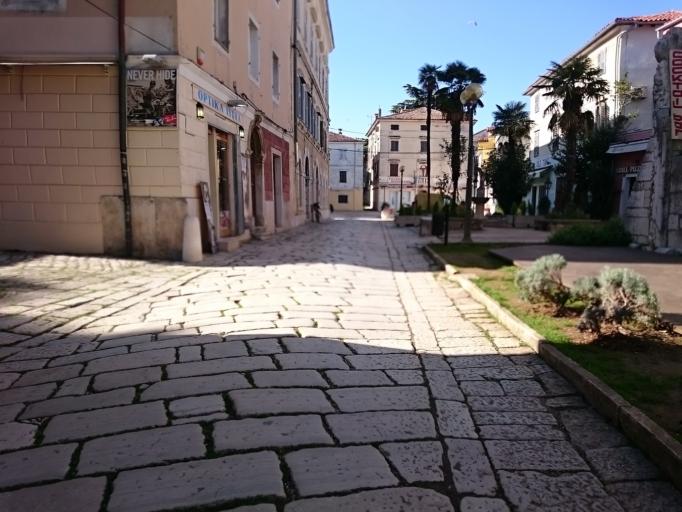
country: HR
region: Istarska
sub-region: Grad Porec
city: Porec
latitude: 45.2281
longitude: 13.5914
